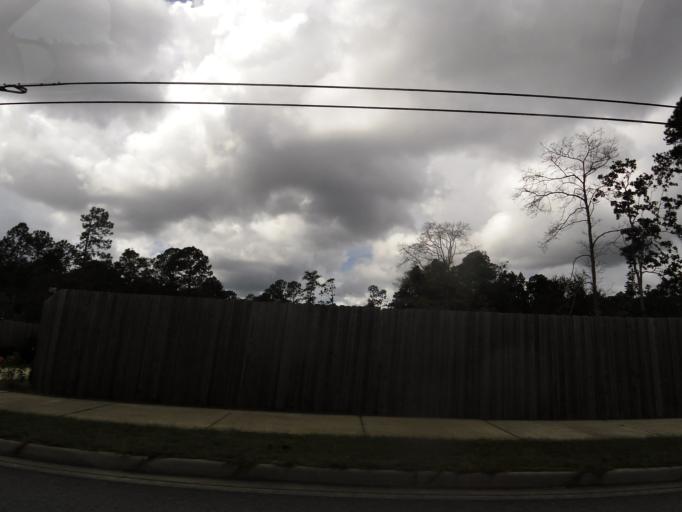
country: US
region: Florida
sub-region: Clay County
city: Asbury Lake
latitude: 30.0574
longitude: -81.8096
